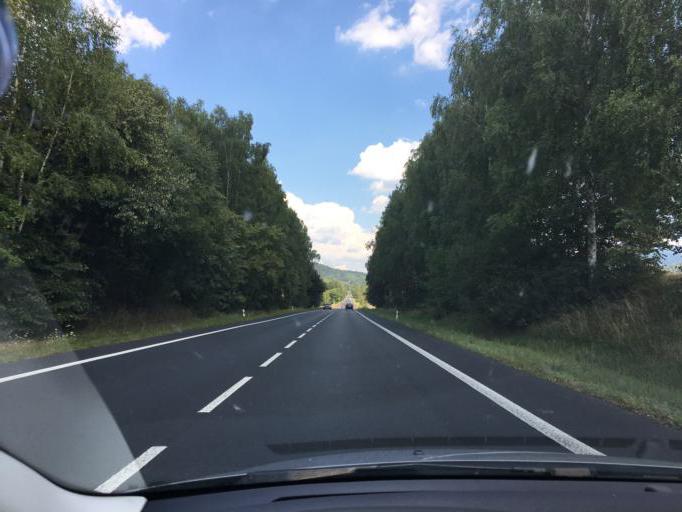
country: CZ
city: Hradek nad Nisou
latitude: 50.7904
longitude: 14.8253
